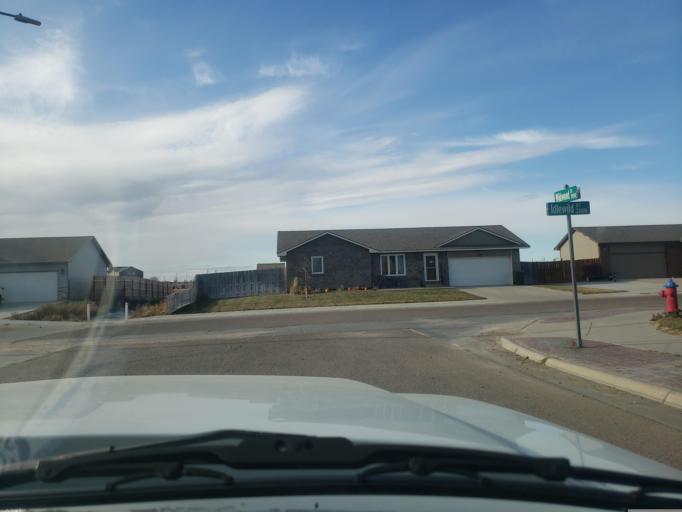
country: US
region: Kansas
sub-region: Finney County
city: Garden City
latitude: 37.9867
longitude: -100.8258
